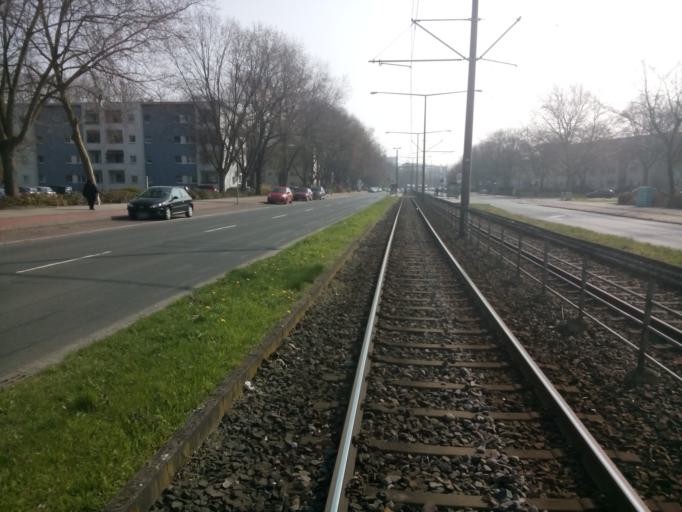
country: DE
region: Lower Saxony
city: Lilienthal
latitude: 53.0793
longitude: 8.8956
